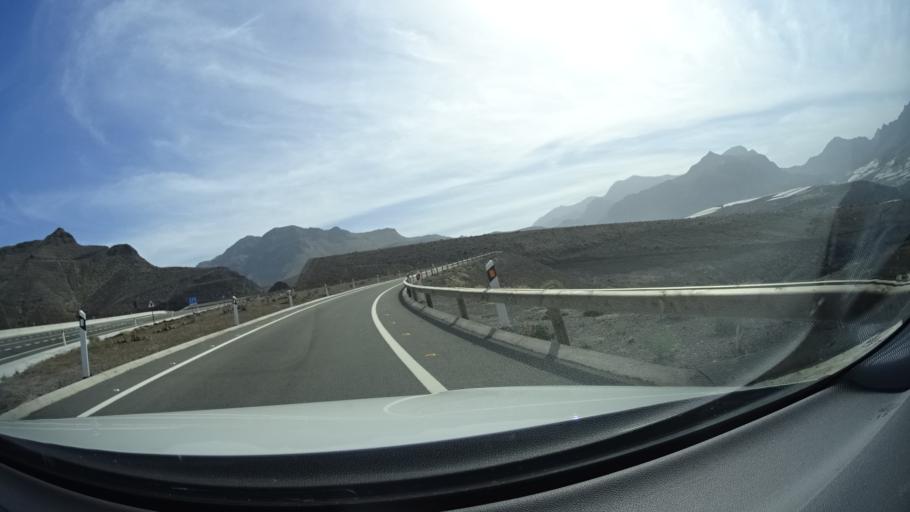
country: ES
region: Canary Islands
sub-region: Provincia de Las Palmas
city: San Nicolas
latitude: 28.0088
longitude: -15.7900
